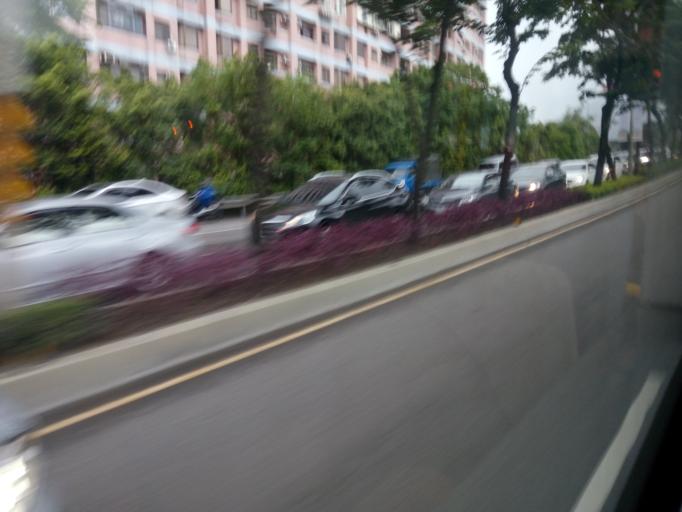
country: TW
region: Taipei
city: Taipei
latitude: 25.0559
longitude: 121.6366
